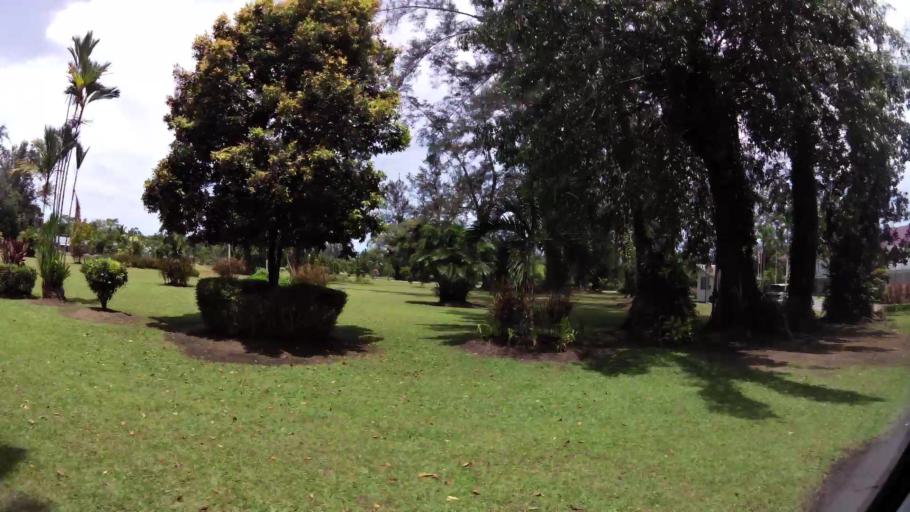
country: BN
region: Belait
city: Kuala Belait
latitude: 4.6015
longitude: 114.2736
